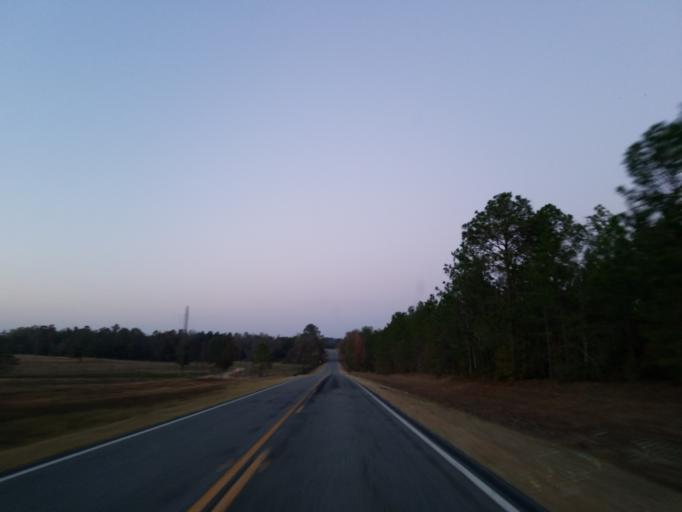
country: US
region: Georgia
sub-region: Wilcox County
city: Rochelle
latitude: 31.8368
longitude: -83.5634
